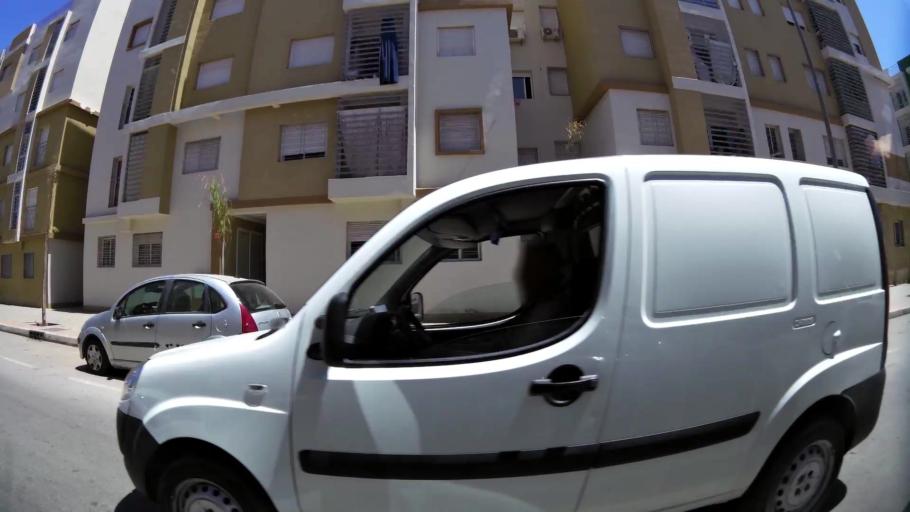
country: MA
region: Oriental
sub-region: Oujda-Angad
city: Oujda
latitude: 34.6618
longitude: -1.9197
